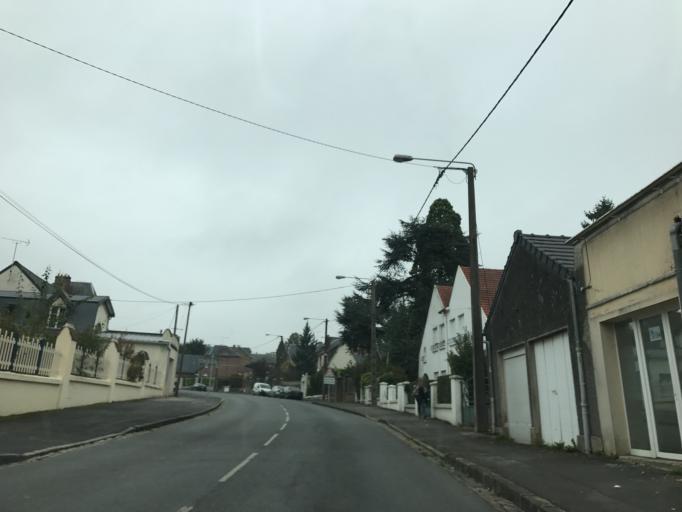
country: FR
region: Picardie
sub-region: Departement de la Somme
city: Peronne
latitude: 49.9313
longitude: 2.9321
